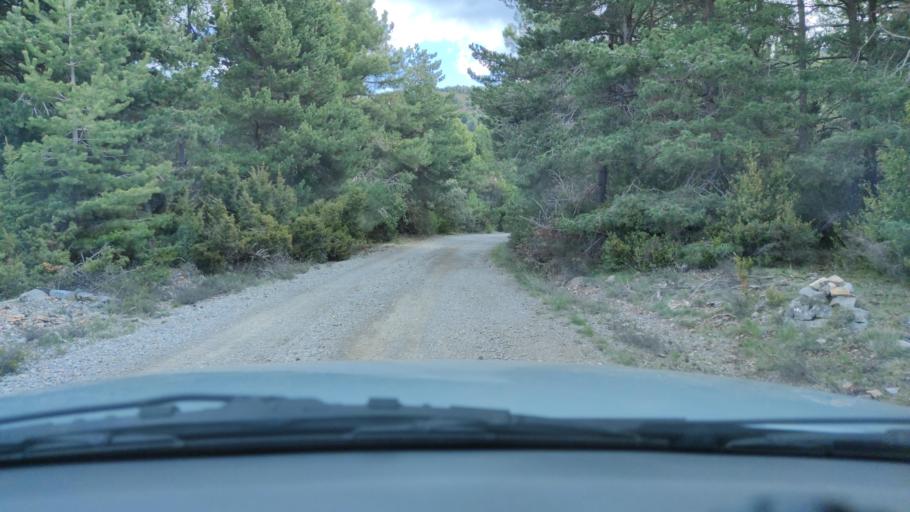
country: ES
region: Catalonia
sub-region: Provincia de Lleida
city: Coll de Nargo
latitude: 42.2520
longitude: 1.4038
